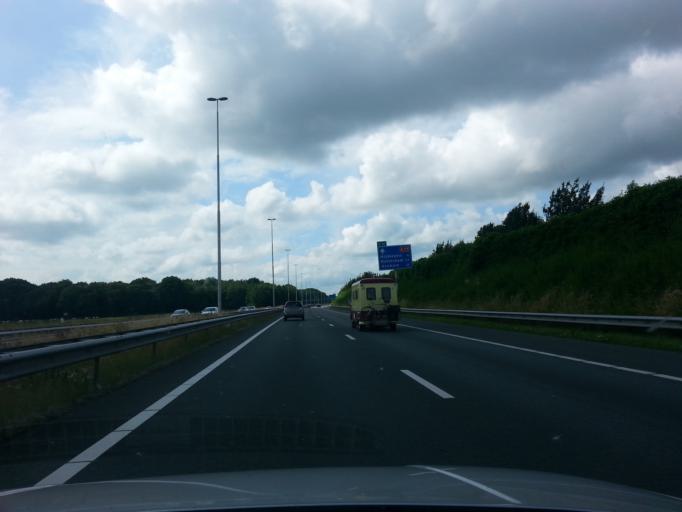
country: NL
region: Gelderland
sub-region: Gemeente Nijmegen
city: Lindenholt
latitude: 51.7923
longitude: 5.8076
